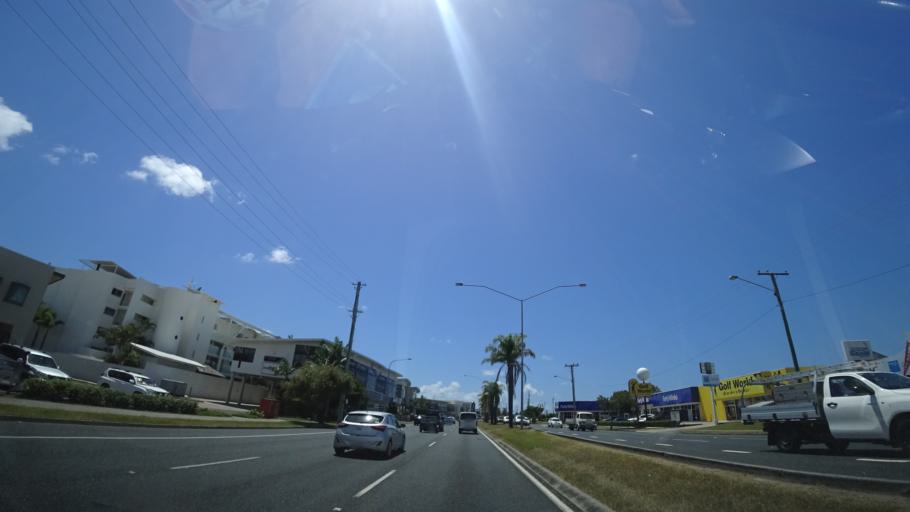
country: AU
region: Queensland
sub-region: Sunshine Coast
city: Mooloolaba
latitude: -26.7006
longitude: 153.1243
